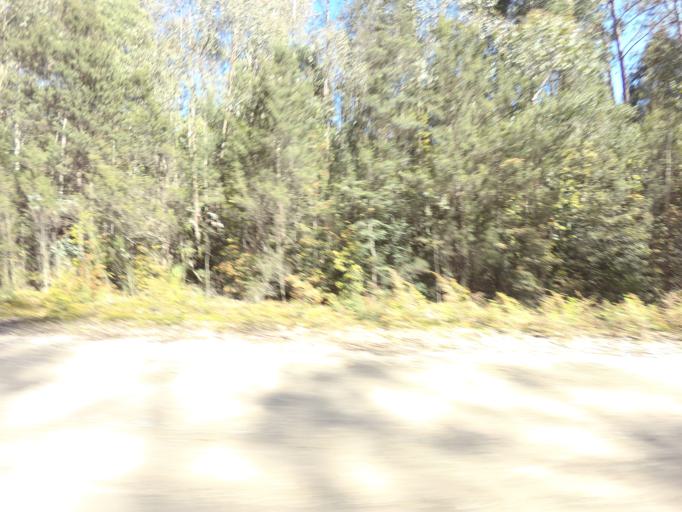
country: AU
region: Tasmania
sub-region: Huon Valley
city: Geeveston
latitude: -42.8670
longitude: 146.3673
